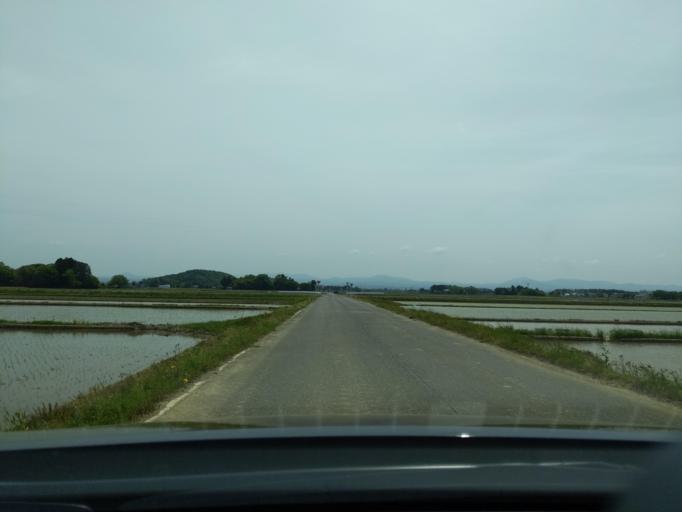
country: JP
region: Fukushima
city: Koriyama
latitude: 37.3983
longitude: 140.2794
